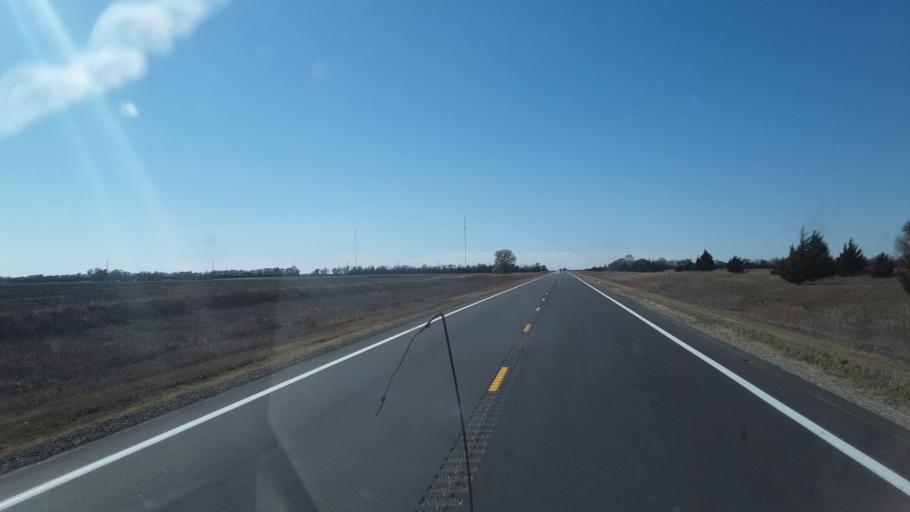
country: US
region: Kansas
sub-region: Rice County
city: Lyons
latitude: 38.3751
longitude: -98.1285
